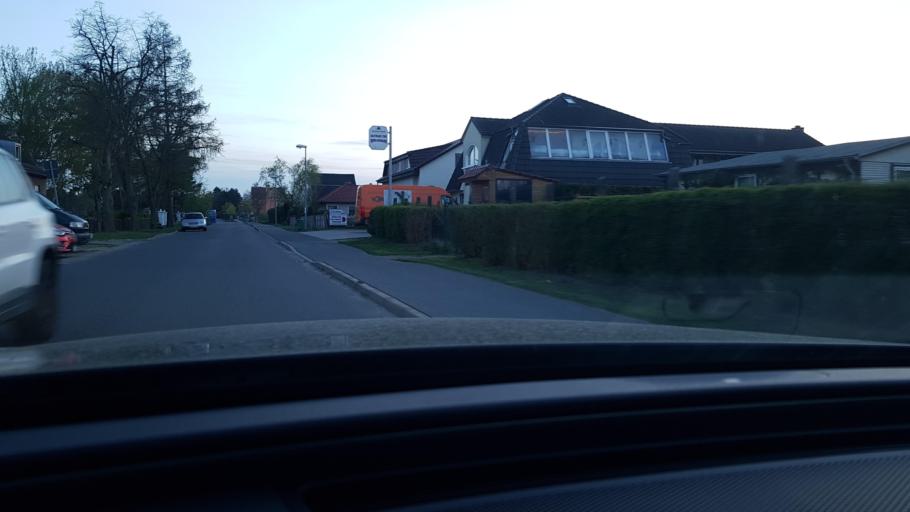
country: DE
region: Berlin
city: Lichtenrade
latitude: 52.3511
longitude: 13.4272
